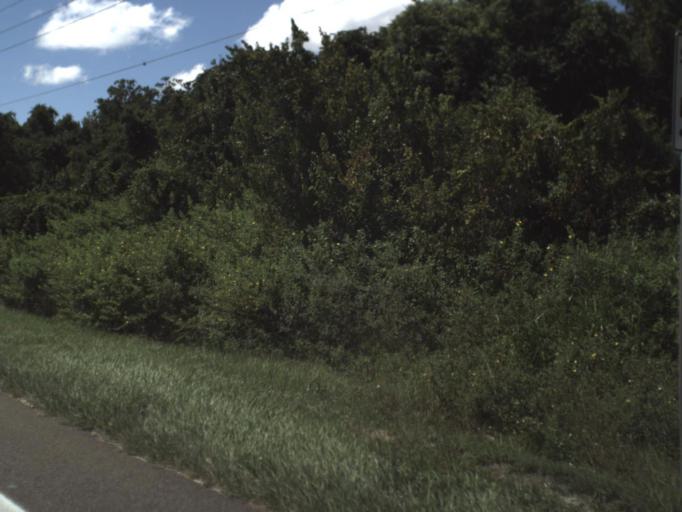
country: US
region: Florida
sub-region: Polk County
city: Lake Hamilton
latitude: 28.0751
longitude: -81.6702
